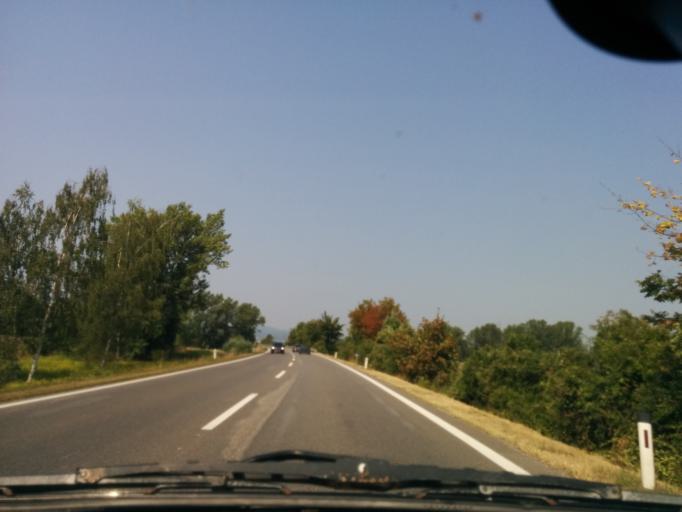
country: AT
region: Lower Austria
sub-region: Politischer Bezirk Krems
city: Grafenegg
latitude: 48.4122
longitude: 15.7108
